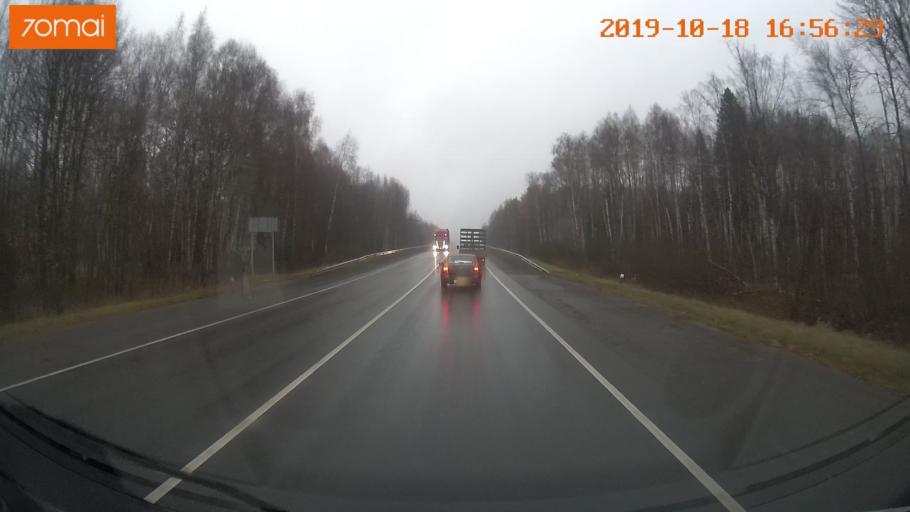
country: RU
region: Ivanovo
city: Novoye Leushino
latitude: 56.6574
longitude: 40.5885
